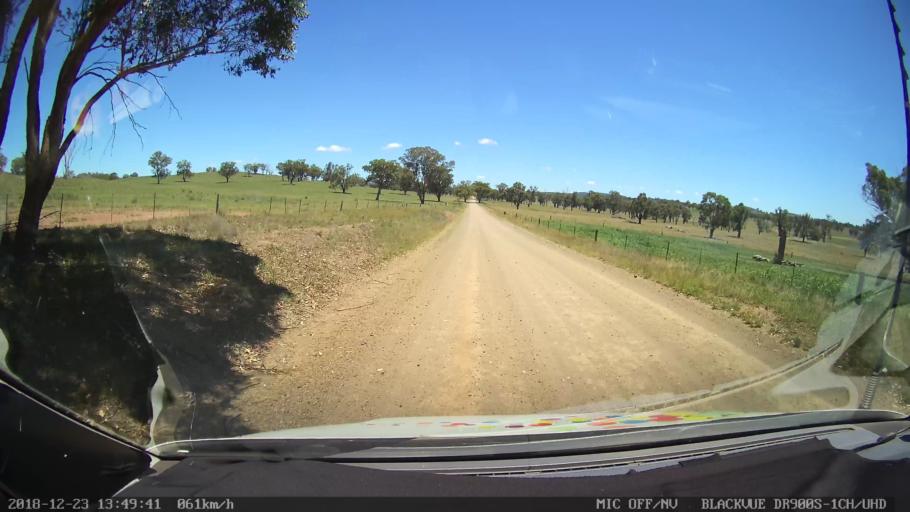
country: AU
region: New South Wales
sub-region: Tamworth Municipality
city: Manilla
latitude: -30.5236
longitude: 151.1080
